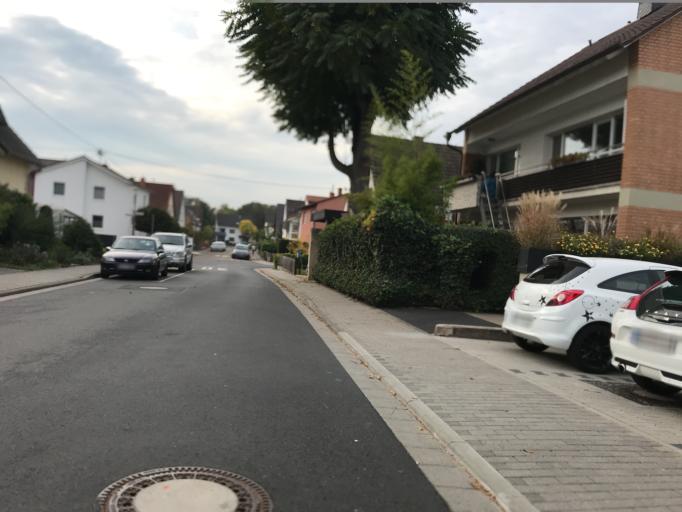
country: DE
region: Rheinland-Pfalz
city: Ingelheim am Rhein
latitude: 49.9716
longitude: 8.0547
